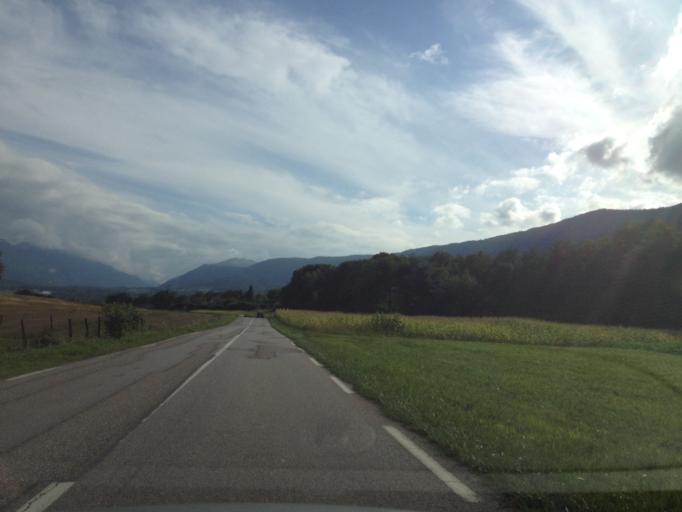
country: FR
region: Rhone-Alpes
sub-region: Departement de la Savoie
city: Le Bourget-du-Lac
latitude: 45.6231
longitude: 5.8622
